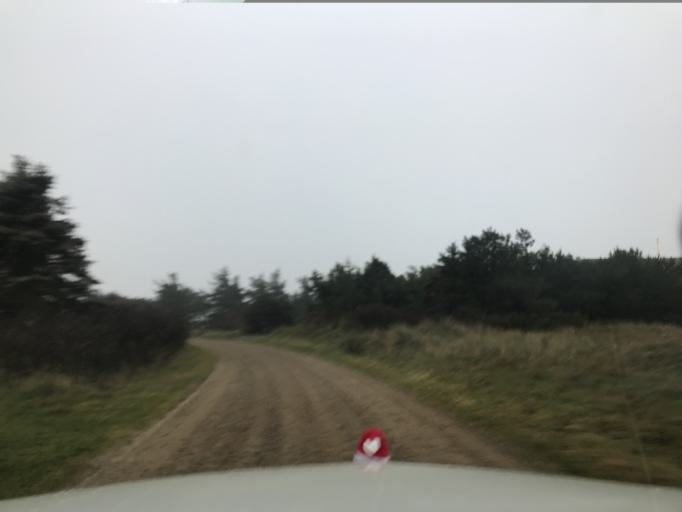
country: DK
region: South Denmark
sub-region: Esbjerg Kommune
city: Tjaereborg
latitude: 55.2710
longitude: 8.5377
